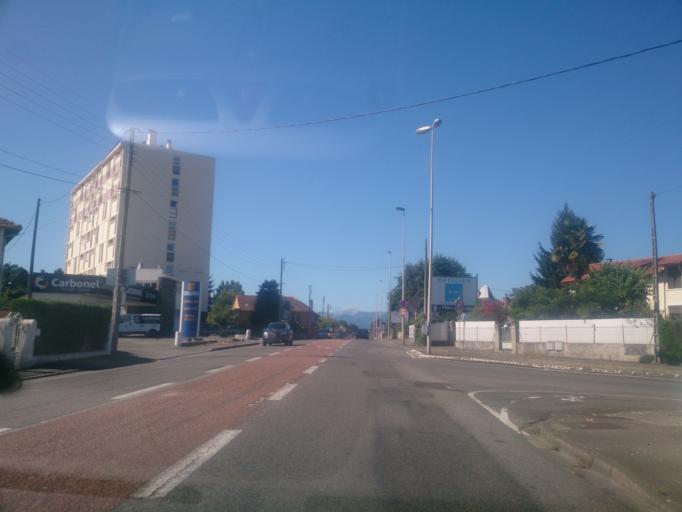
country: FR
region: Midi-Pyrenees
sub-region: Departement des Hautes-Pyrenees
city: Laloubere
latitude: 43.2188
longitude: 0.0579
